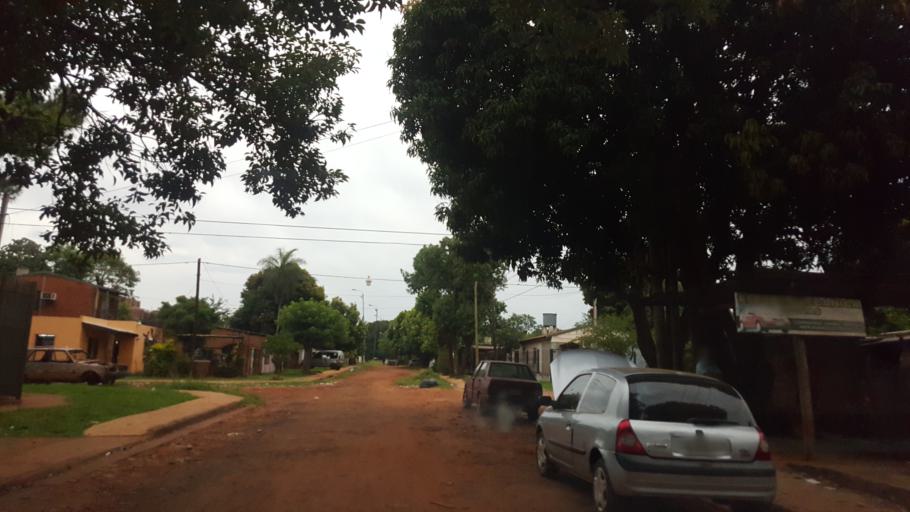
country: AR
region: Misiones
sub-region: Departamento de Capital
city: Posadas
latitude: -27.3685
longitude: -55.9270
